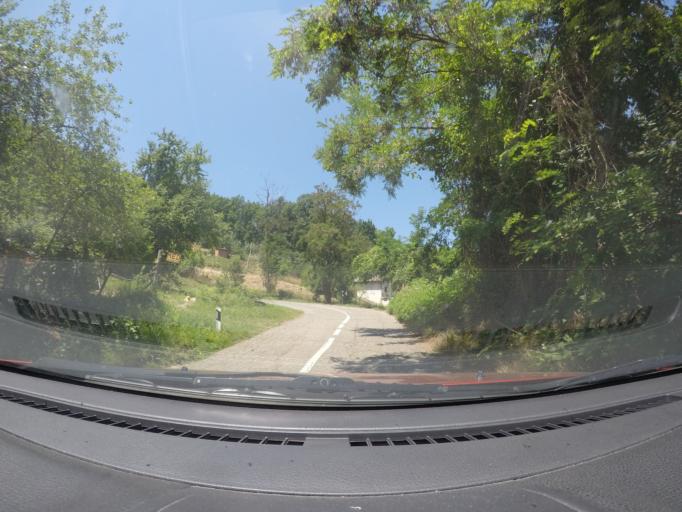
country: RO
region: Mehedinti
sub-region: Comuna Svinita
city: Svinita
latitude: 44.4740
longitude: 22.1003
